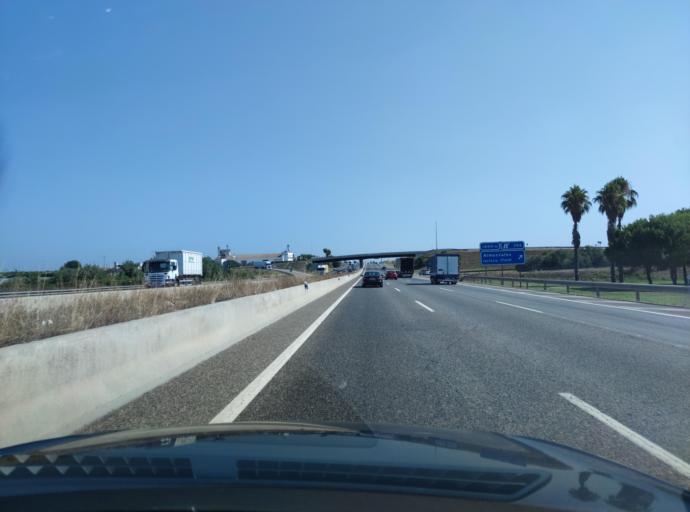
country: ES
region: Valencia
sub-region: Provincia de Valencia
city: Benifaio
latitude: 39.3228
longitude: -0.4368
